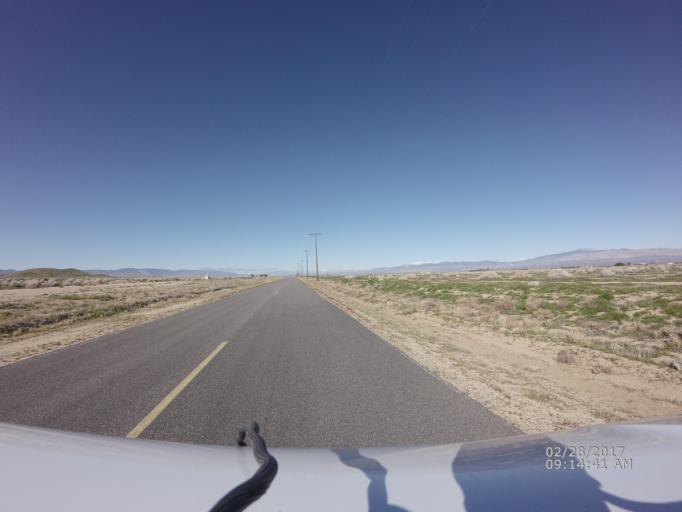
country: US
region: California
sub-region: Kern County
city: Rosamond
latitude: 34.8056
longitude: -118.2939
